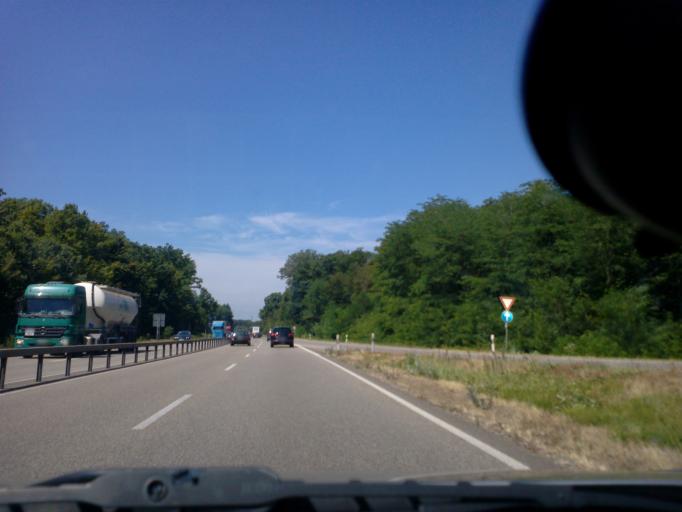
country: DE
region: Baden-Wuerttemberg
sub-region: Freiburg Region
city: Offenburg
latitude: 48.4705
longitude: 7.9188
